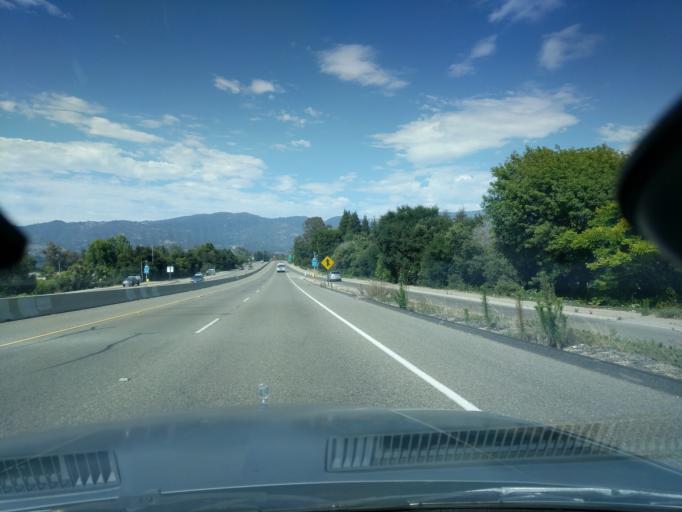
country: US
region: California
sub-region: Santa Barbara County
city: Goleta
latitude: 34.4367
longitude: -119.8168
